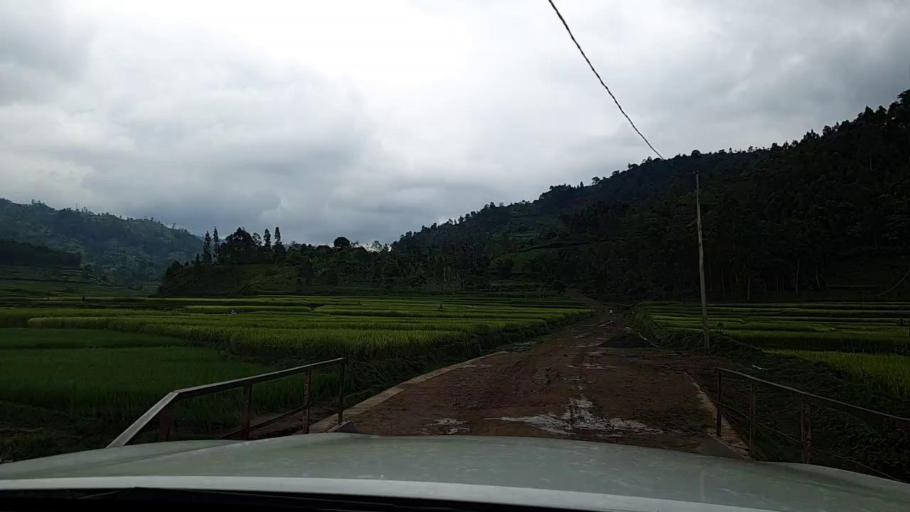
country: RW
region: Western Province
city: Cyangugu
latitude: -2.5650
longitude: 29.0352
